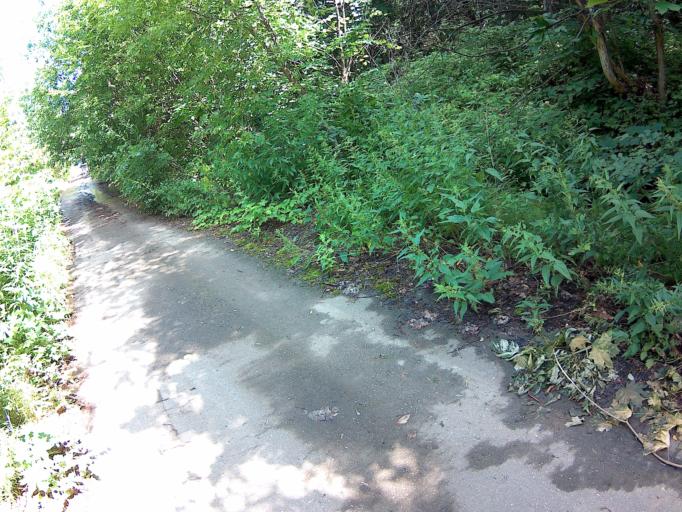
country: RU
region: Nizjnij Novgorod
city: Nizhniy Novgorod
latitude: 56.2359
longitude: 43.9345
